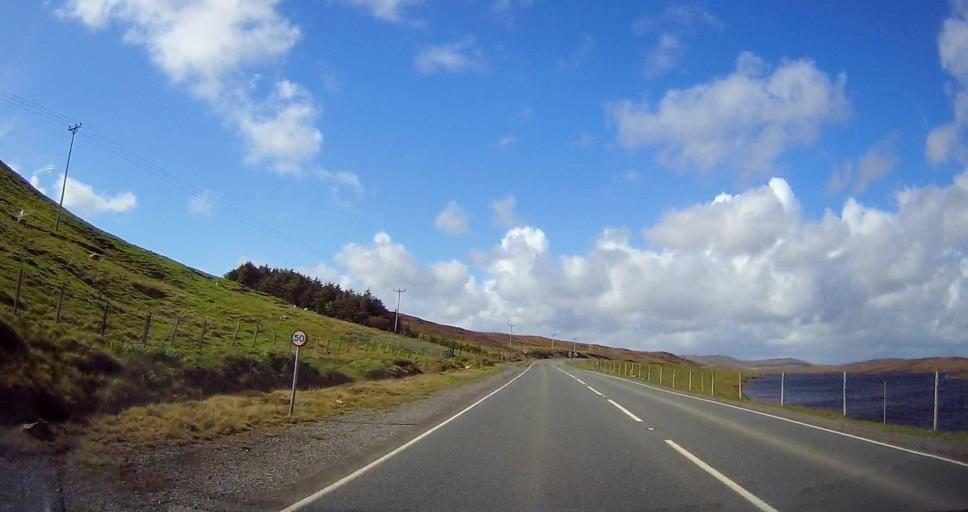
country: GB
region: Scotland
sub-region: Shetland Islands
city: Lerwick
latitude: 60.2407
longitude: -1.2286
